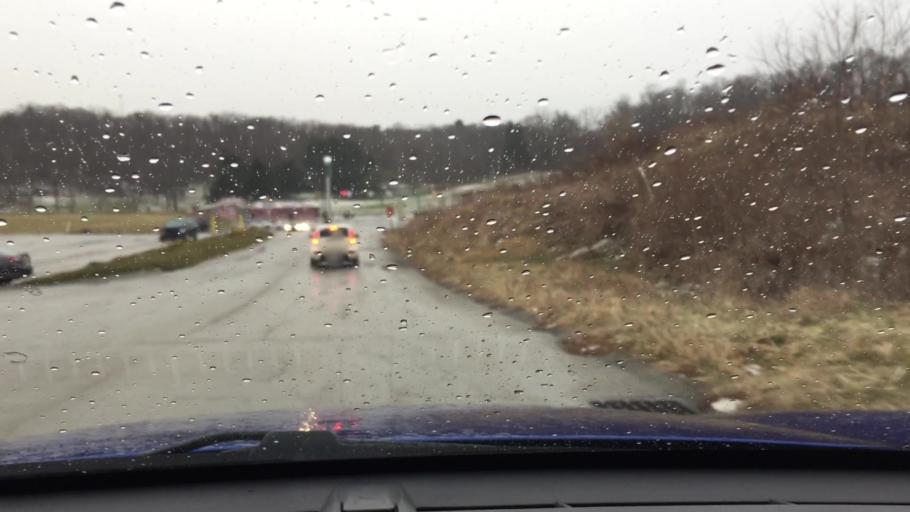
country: US
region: Pennsylvania
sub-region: Westmoreland County
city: Fellsburg
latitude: 40.1860
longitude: -79.8112
